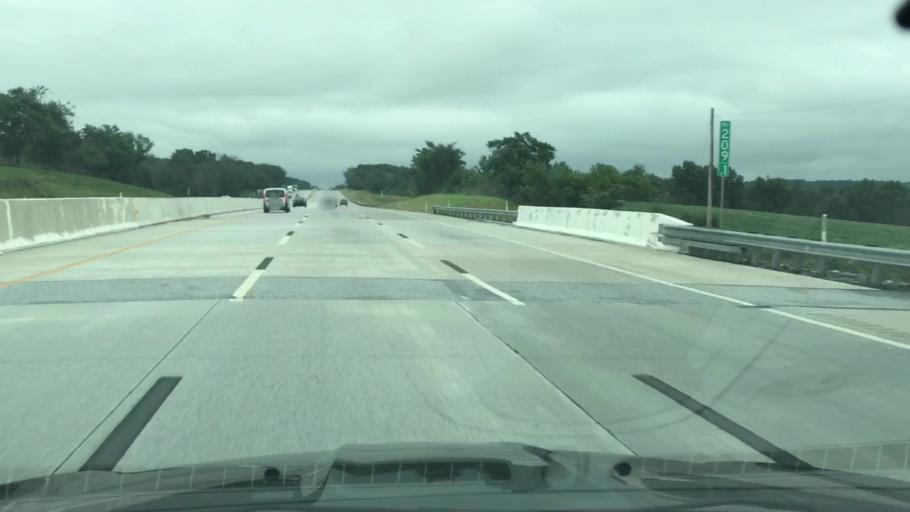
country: US
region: Pennsylvania
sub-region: Cumberland County
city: Newville
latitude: 40.1858
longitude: -77.4747
